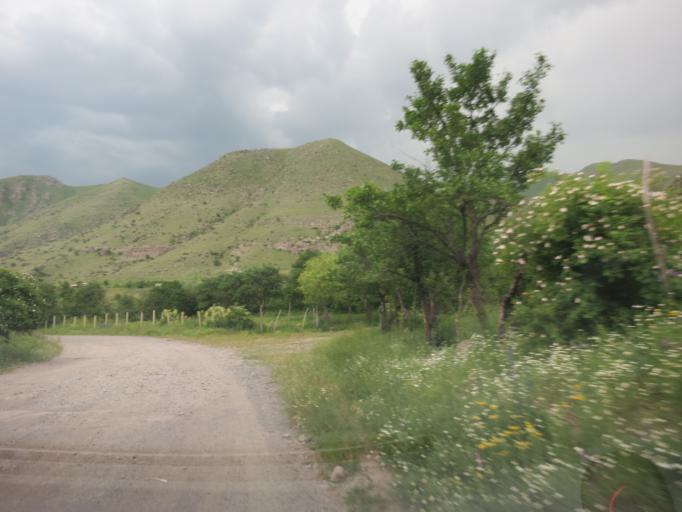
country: TR
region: Ardahan
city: Kurtkale
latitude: 41.3730
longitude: 43.2624
